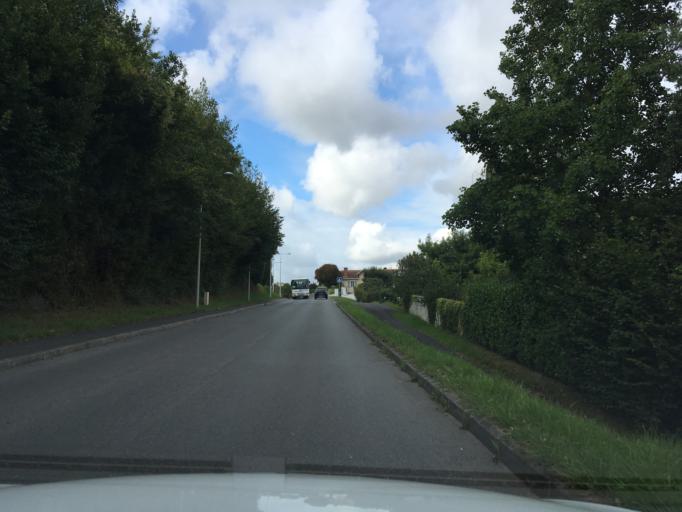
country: FR
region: Aquitaine
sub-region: Departement des Pyrenees-Atlantiques
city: Bassussarry
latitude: 43.4563
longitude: -1.4971
